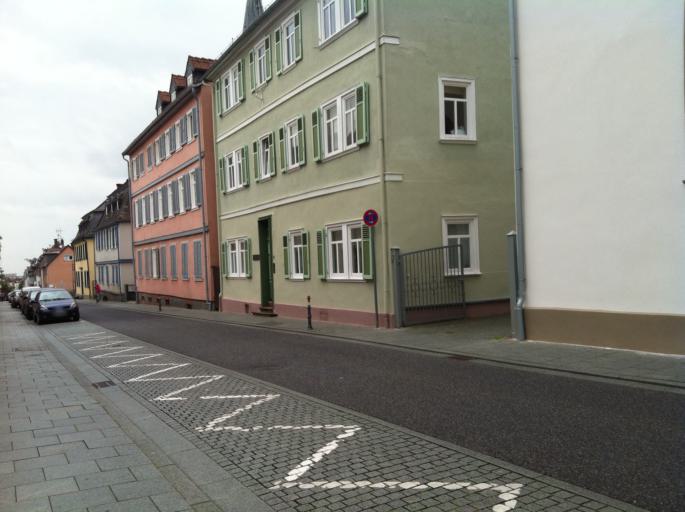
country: DE
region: Hesse
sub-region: Regierungsbezirk Darmstadt
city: Bad Homburg vor der Hoehe
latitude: 50.2269
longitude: 8.6128
